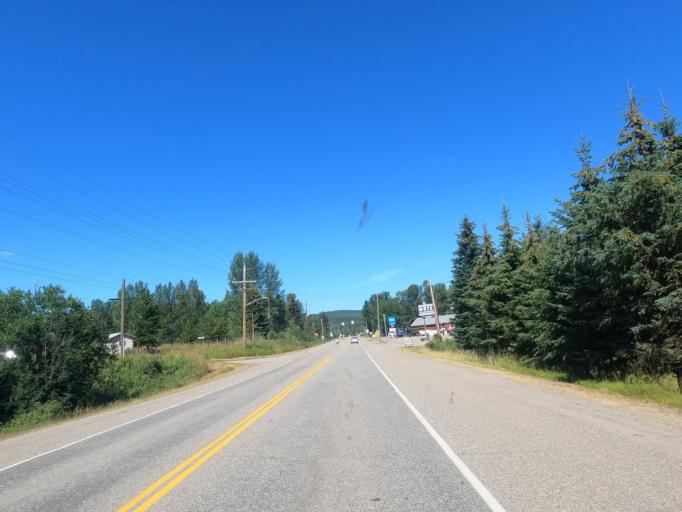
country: CA
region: British Columbia
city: Quesnel
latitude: 53.4184
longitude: -122.5838
